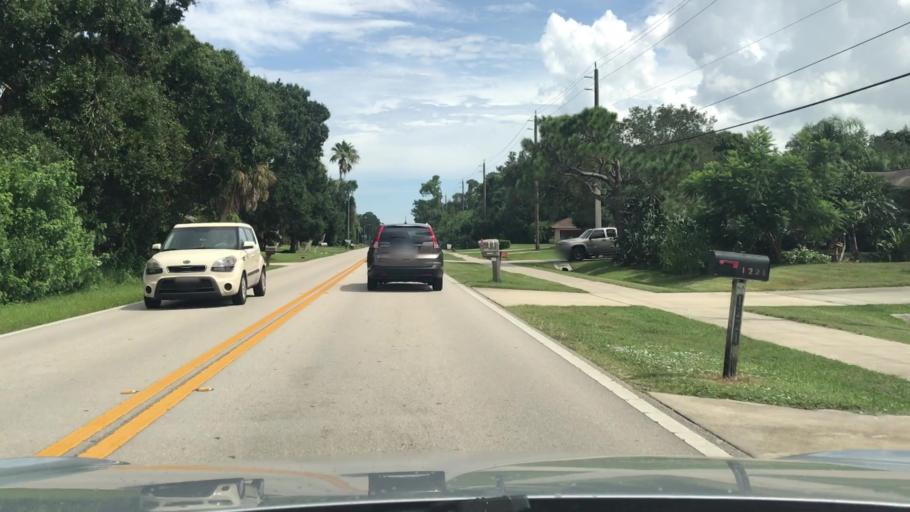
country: US
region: Florida
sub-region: Indian River County
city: Sebastian
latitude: 27.7745
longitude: -80.4837
